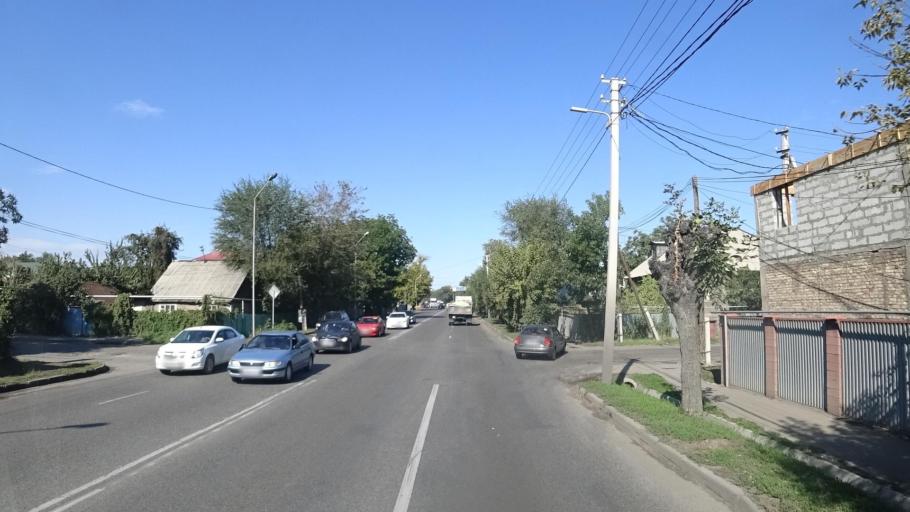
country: KZ
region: Almaty Oblysy
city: Pervomayskiy
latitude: 43.3540
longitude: 76.9514
